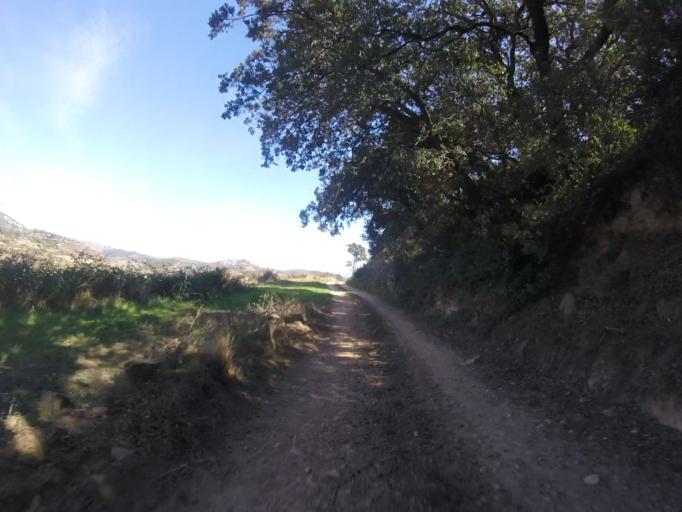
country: ES
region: Valencia
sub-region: Provincia de Castello
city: Sierra-Engarceran
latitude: 40.2733
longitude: -0.0002
